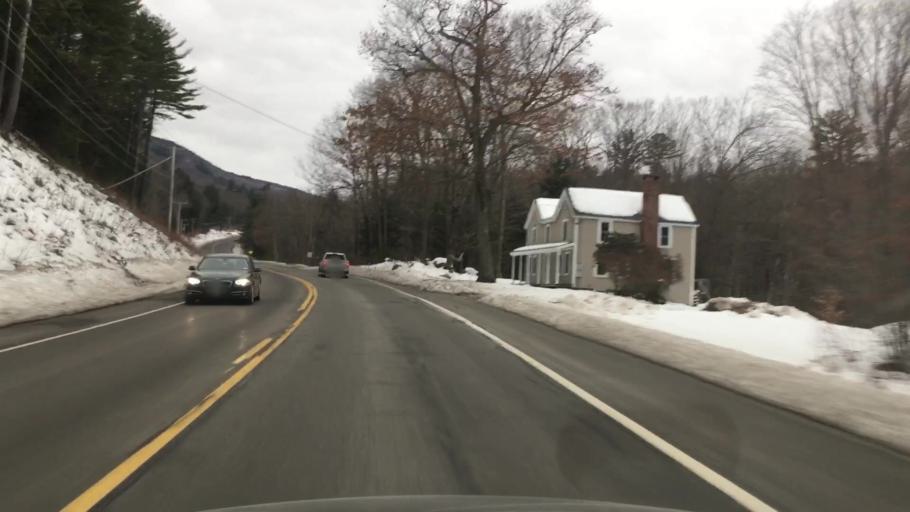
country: US
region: New Hampshire
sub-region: Merrimack County
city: Newbury
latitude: 43.3107
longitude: -72.0205
